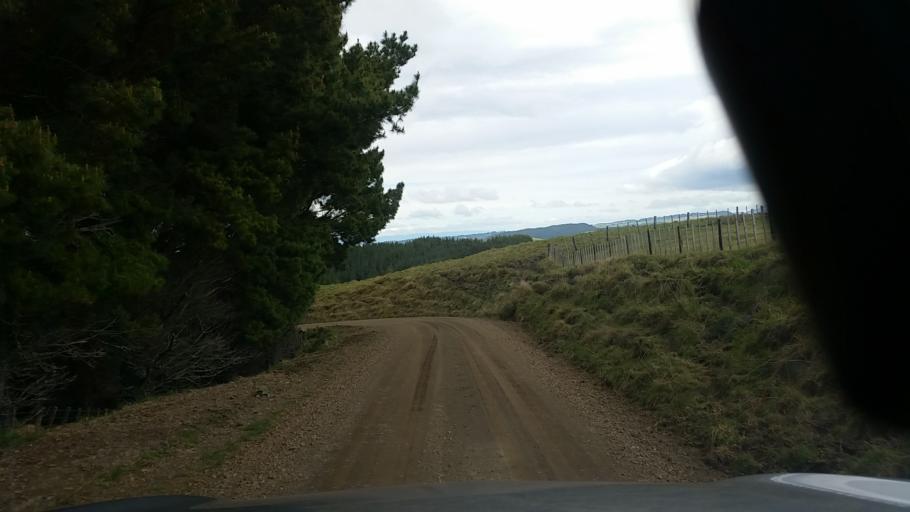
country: NZ
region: Hawke's Bay
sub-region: Napier City
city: Napier
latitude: -39.2174
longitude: 176.9796
